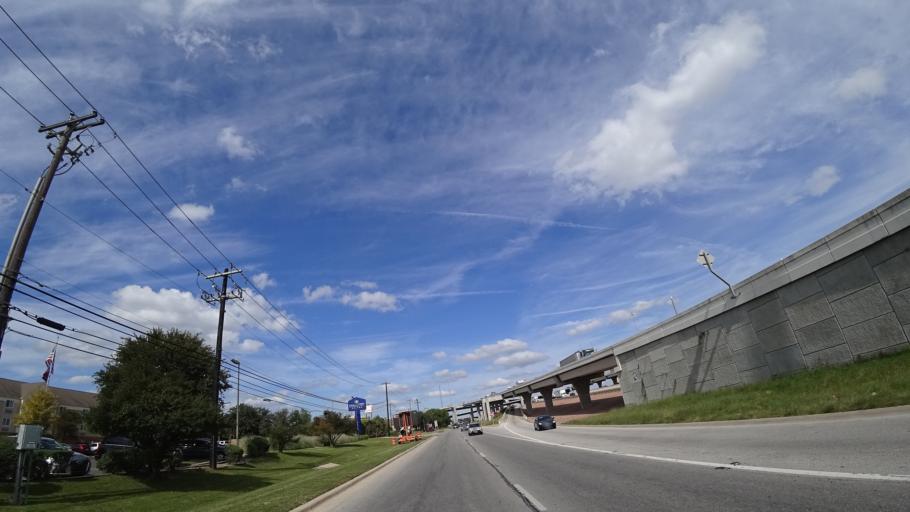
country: US
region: Texas
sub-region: Travis County
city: Austin
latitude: 30.2121
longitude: -97.7547
